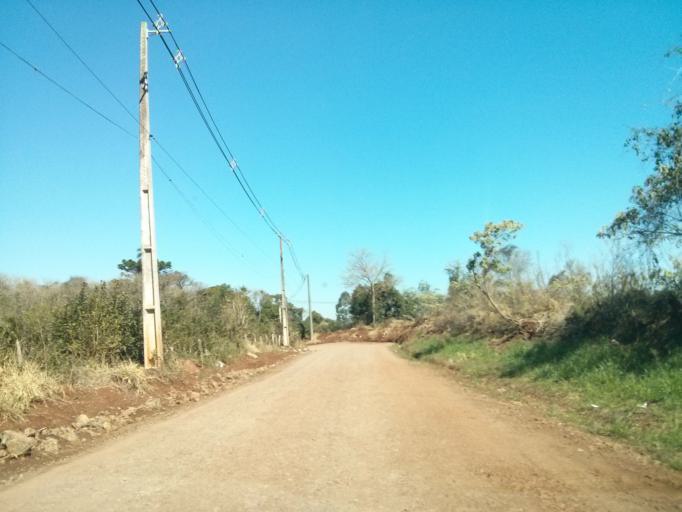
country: BR
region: Santa Catarina
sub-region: Chapeco
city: Chapeco
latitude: -27.0936
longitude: -52.6941
